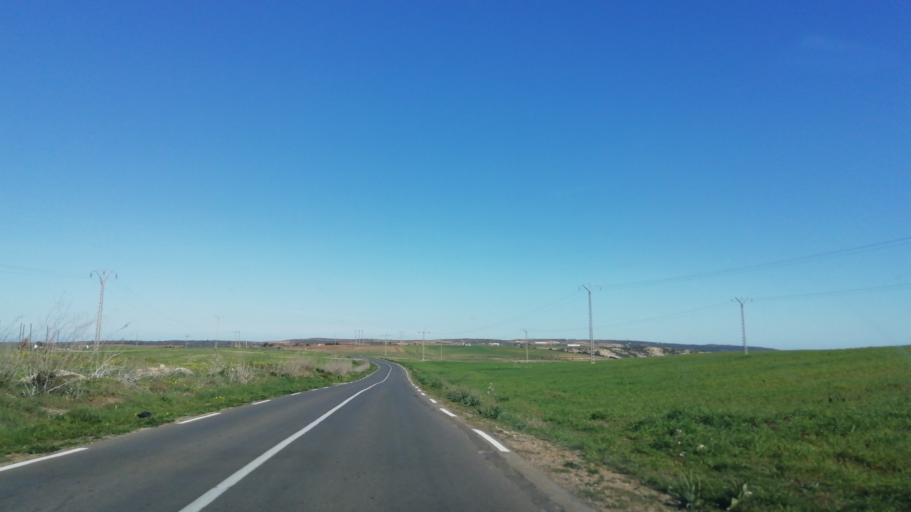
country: DZ
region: Oran
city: Bou Tlelis
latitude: 35.6456
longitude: -0.9462
